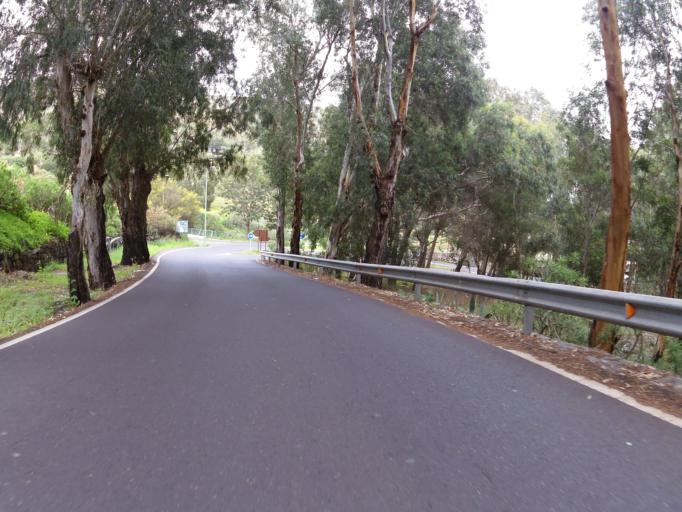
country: ES
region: Canary Islands
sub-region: Provincia de Las Palmas
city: Arucas
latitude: 28.1015
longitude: -15.5309
